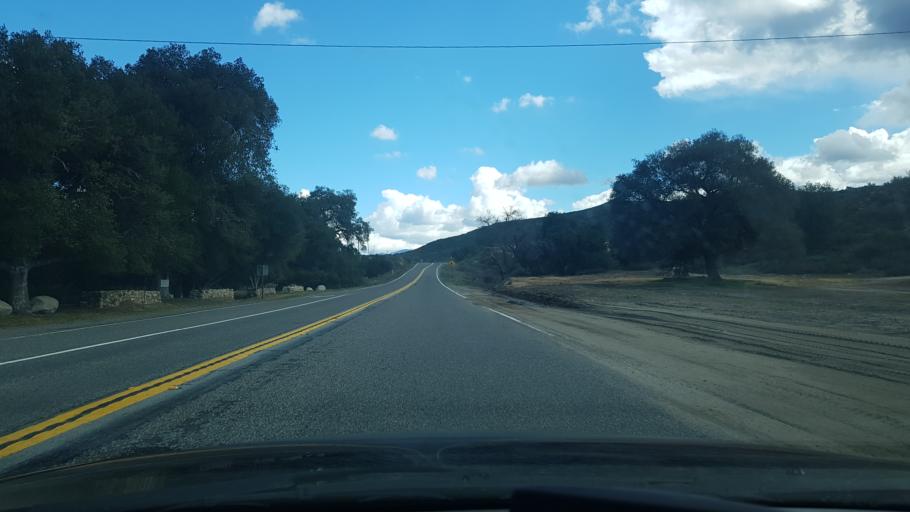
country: US
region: California
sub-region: Riverside County
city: Aguanga
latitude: 33.4681
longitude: -116.9978
